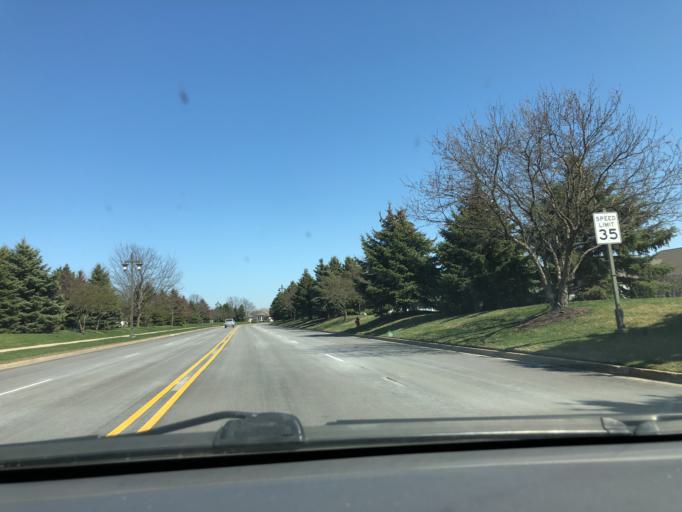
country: US
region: Illinois
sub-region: McHenry County
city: Huntley
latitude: 42.1556
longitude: -88.4498
